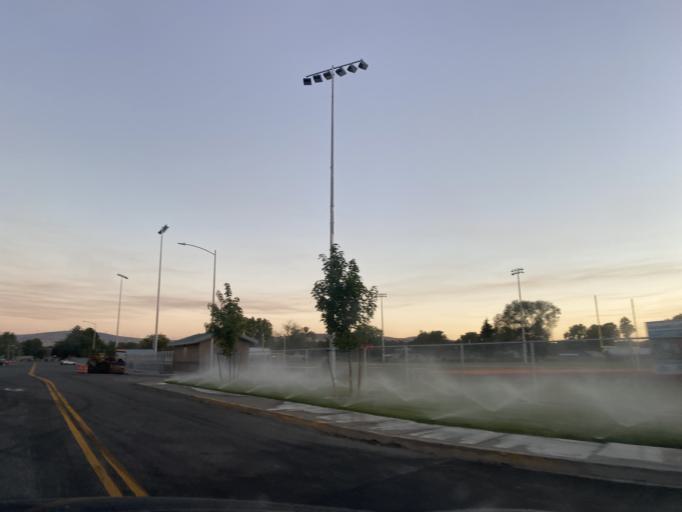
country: US
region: Washington
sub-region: Benton County
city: Kennewick
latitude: 46.2027
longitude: -119.1230
